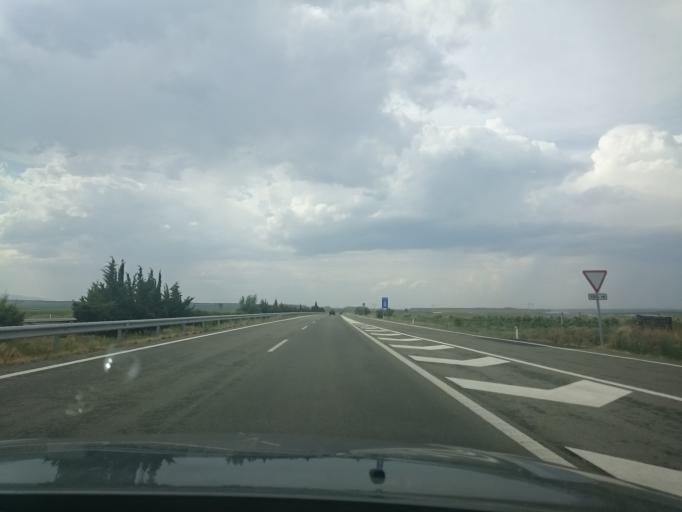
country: ES
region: Navarre
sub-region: Provincia de Navarra
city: Corella
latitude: 42.1658
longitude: -1.8274
